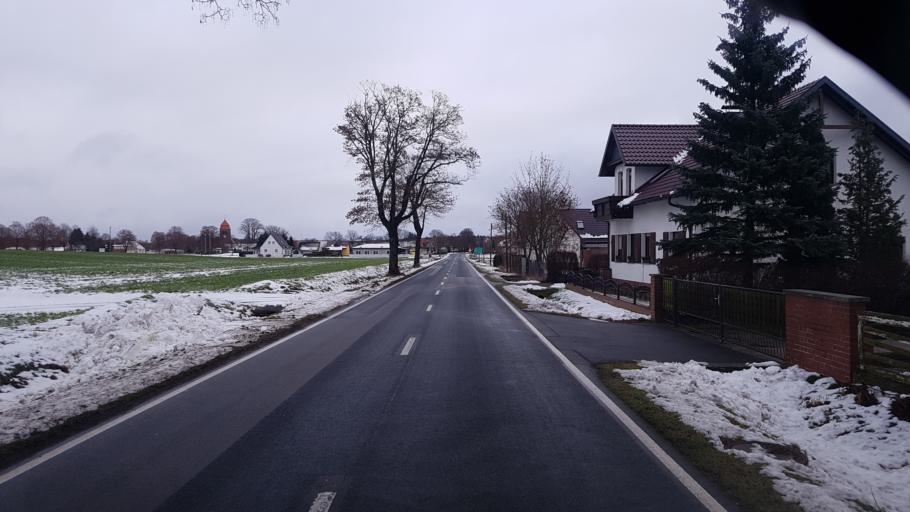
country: DE
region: Brandenburg
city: Schenkendobern
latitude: 51.9784
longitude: 14.5298
